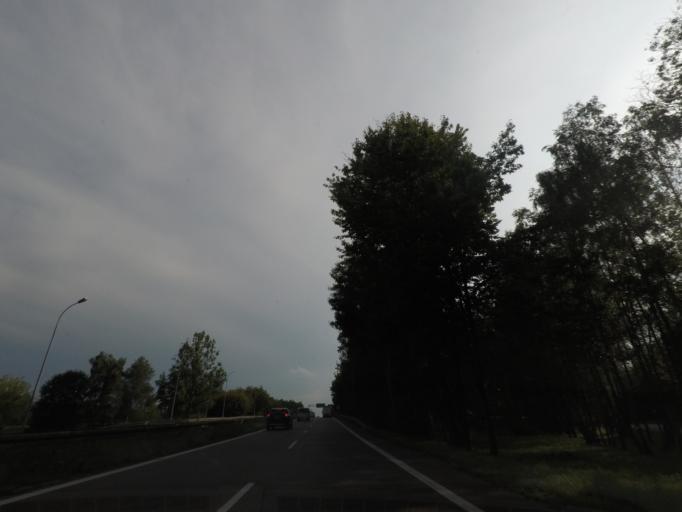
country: PL
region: Silesian Voivodeship
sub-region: Dabrowa Gornicza
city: Dabrowa Gornicza
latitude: 50.3199
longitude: 19.2380
